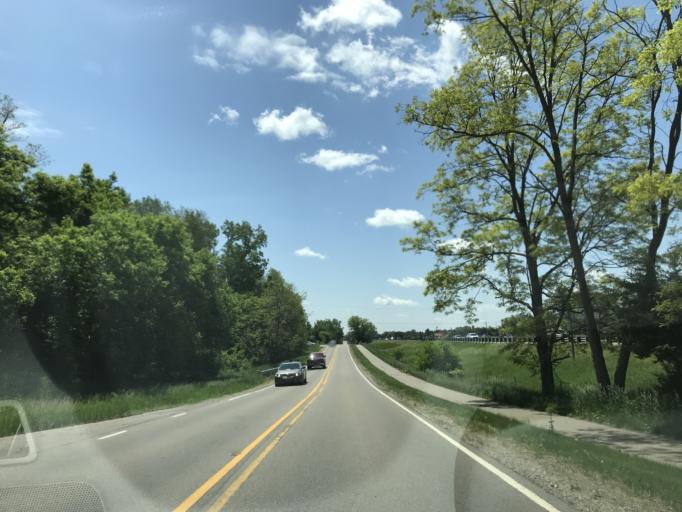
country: US
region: Michigan
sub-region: Livingston County
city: Brighton
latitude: 42.4989
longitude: -83.7572
